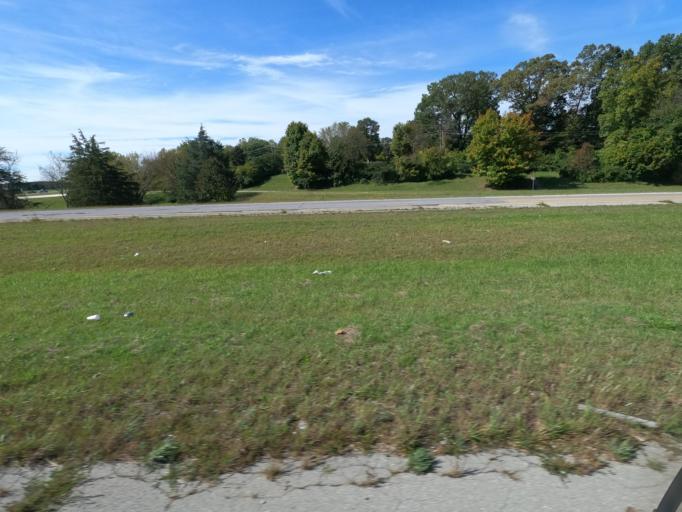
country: US
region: Tennessee
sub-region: Hamblen County
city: Morristown
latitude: 36.2295
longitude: -83.2594
